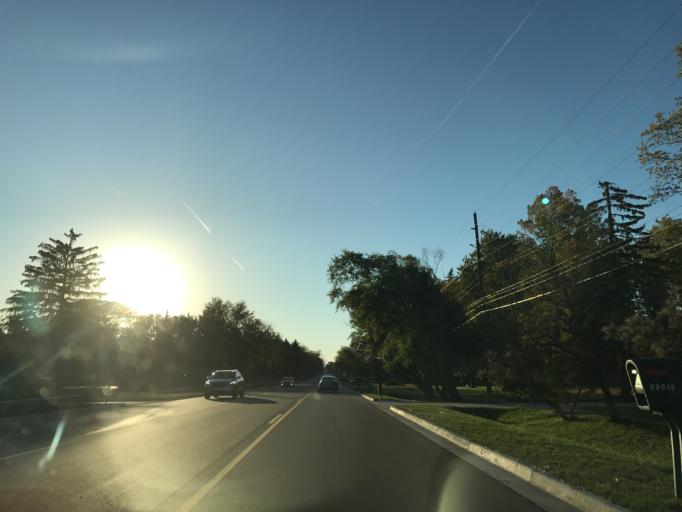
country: US
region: Michigan
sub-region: Oakland County
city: Farmington Hills
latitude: 42.4851
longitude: -83.3433
